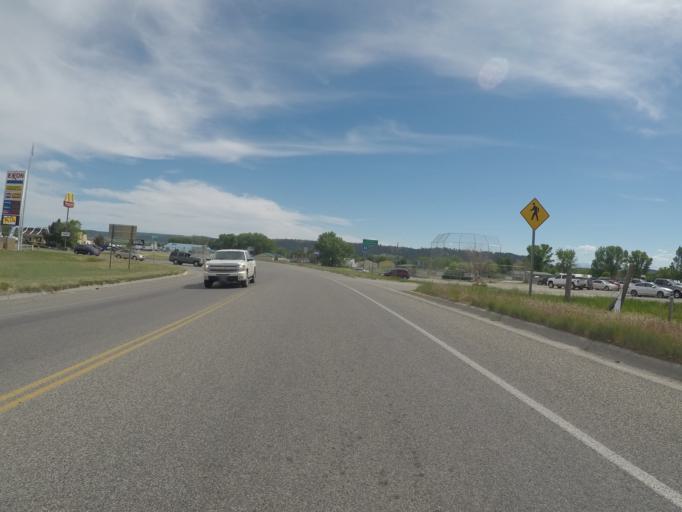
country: US
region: Montana
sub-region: Stillwater County
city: Columbus
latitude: 45.6453
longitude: -109.2487
